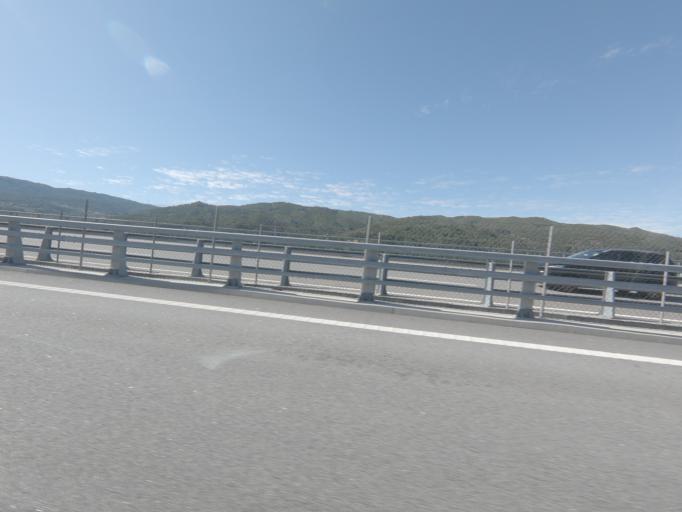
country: PT
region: Porto
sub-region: Baiao
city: Valadares
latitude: 41.2516
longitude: -7.9666
